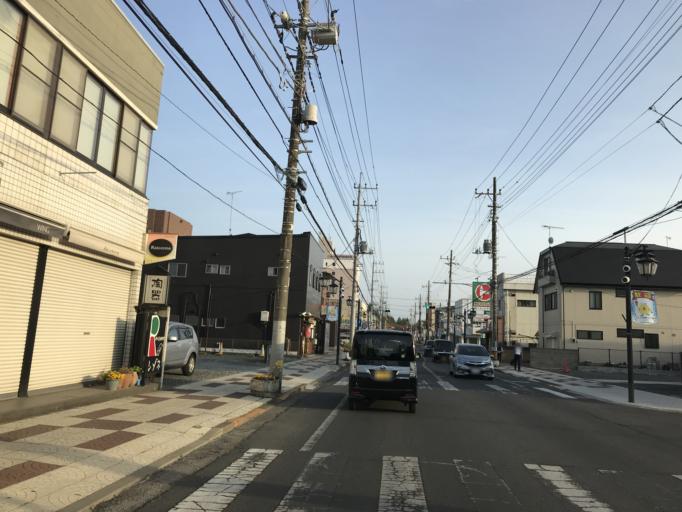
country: JP
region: Ibaraki
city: Katsuta
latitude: 36.3885
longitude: 140.5272
